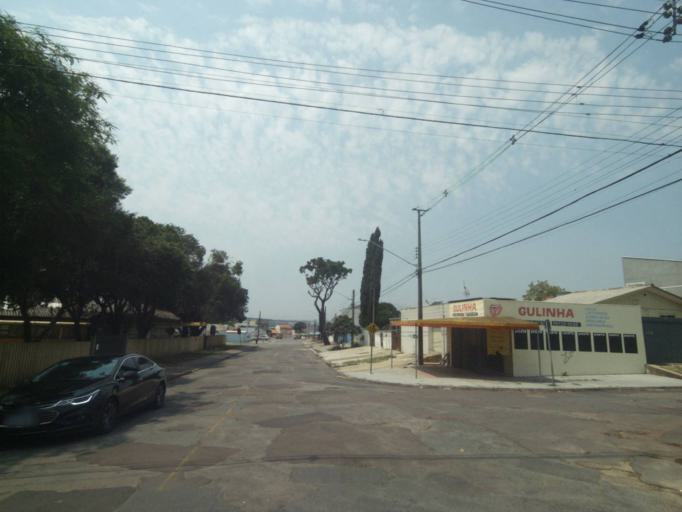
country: BR
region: Parana
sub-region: Sao Jose Dos Pinhais
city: Sao Jose dos Pinhais
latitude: -25.5364
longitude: -49.2439
